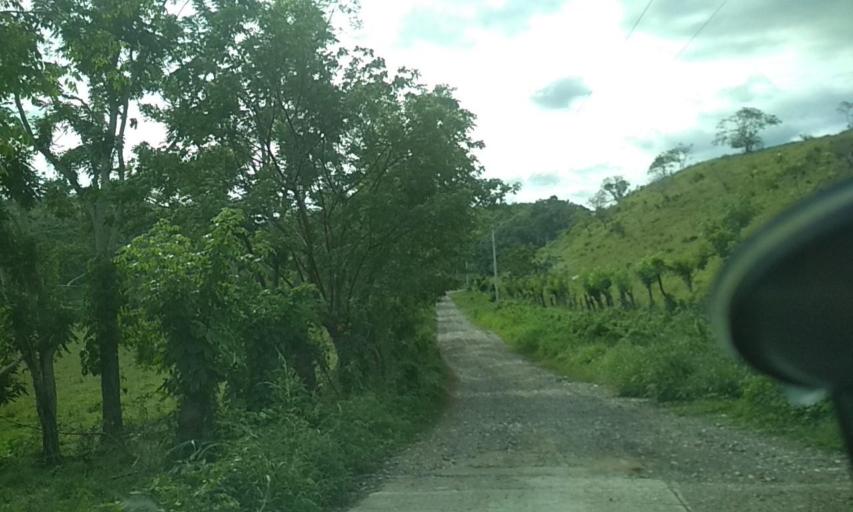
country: MX
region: Veracruz
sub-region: Papantla
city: Polutla
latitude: 20.5669
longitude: -97.1965
